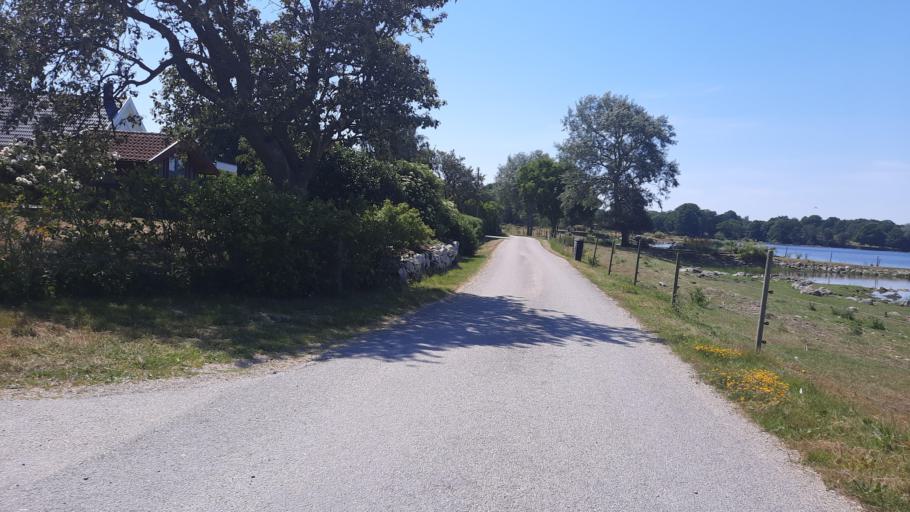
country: SE
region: Blekinge
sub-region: Karlskrona Kommun
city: Jaemjoe
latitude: 56.1567
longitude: 15.7593
